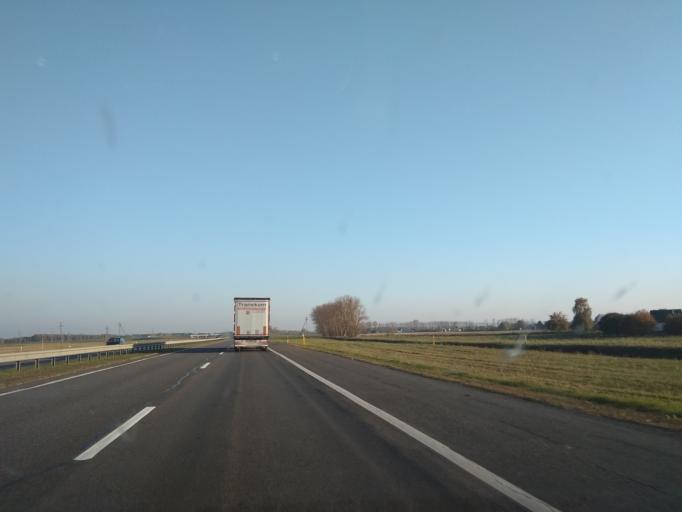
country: BY
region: Brest
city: Kobryn
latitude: 52.1892
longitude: 24.3135
